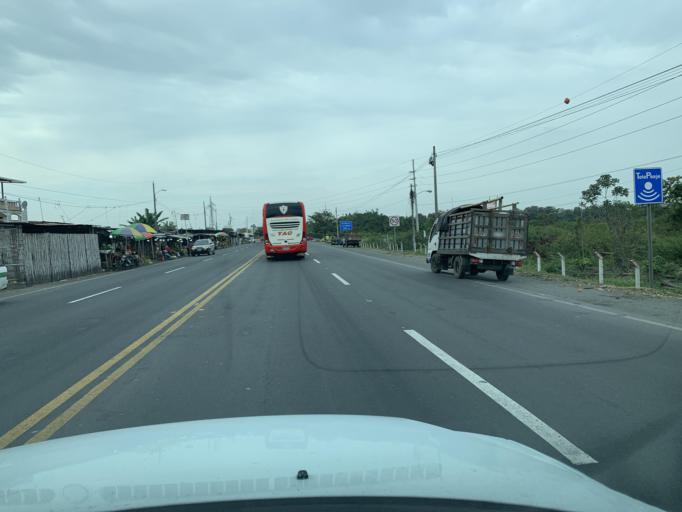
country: EC
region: Guayas
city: Yaguachi Nuevo
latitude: -2.2382
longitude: -79.6386
